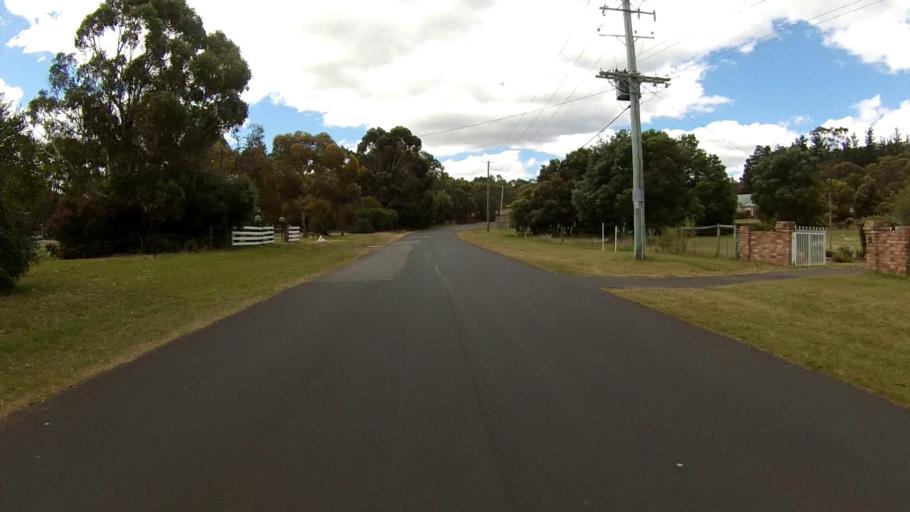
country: AU
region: Tasmania
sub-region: Clarence
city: Acton Park
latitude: -42.8808
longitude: 147.4891
